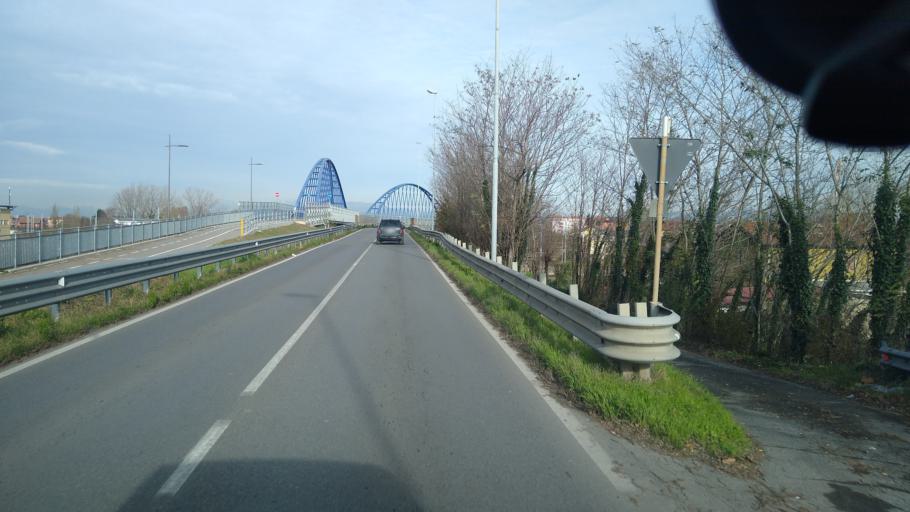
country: IT
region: Lombardy
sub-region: Provincia di Bergamo
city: Treviglio
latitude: 45.5137
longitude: 9.5823
